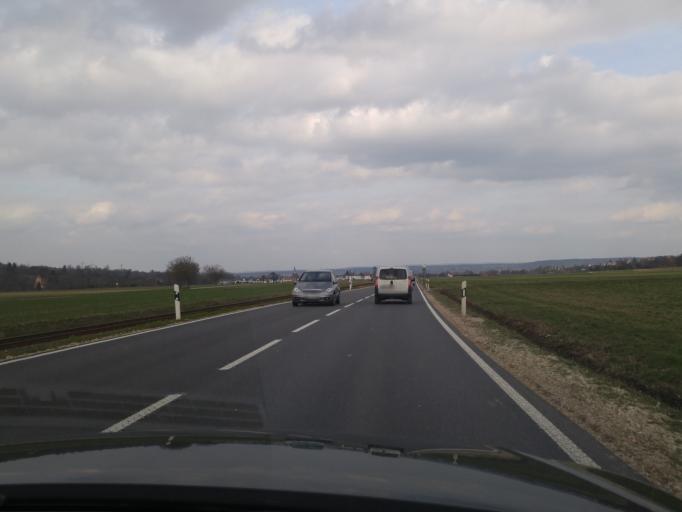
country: DE
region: Baden-Wuerttemberg
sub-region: Regierungsbezirk Stuttgart
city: Owen
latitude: 48.5983
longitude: 9.4494
